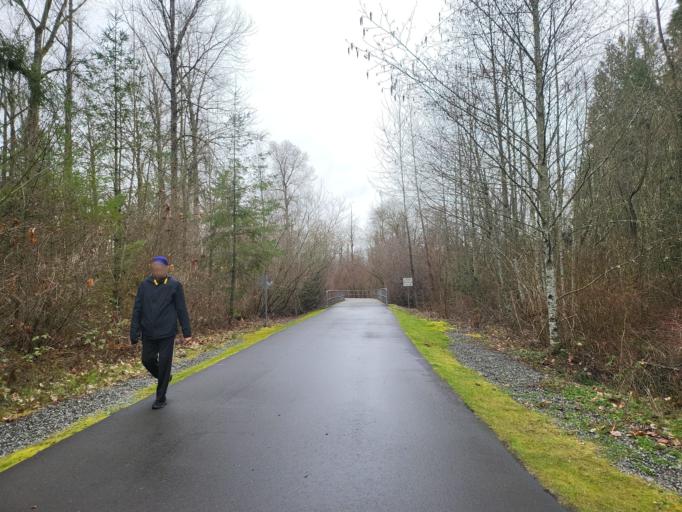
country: US
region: Washington
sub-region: King County
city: East Hill-Meridian
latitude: 47.4177
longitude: -122.1603
